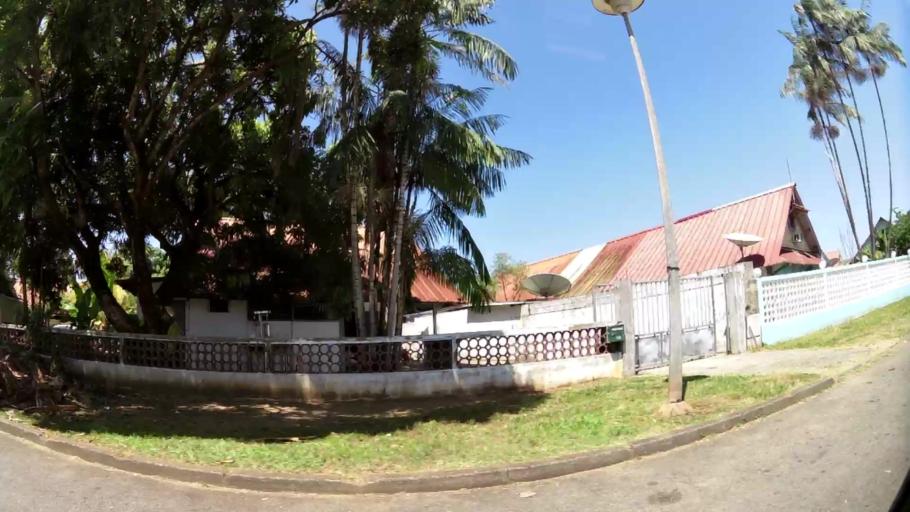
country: GF
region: Guyane
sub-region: Guyane
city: Kourou
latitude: 5.1694
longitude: -52.6542
